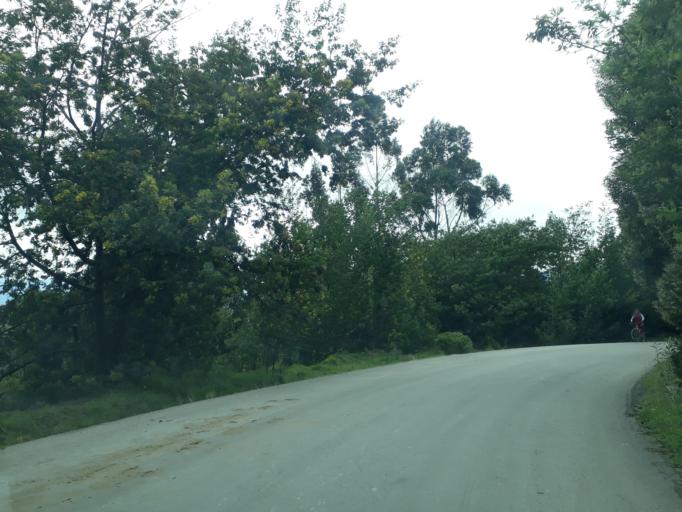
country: CO
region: Cundinamarca
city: Cucunuba
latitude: 5.2104
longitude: -73.7855
